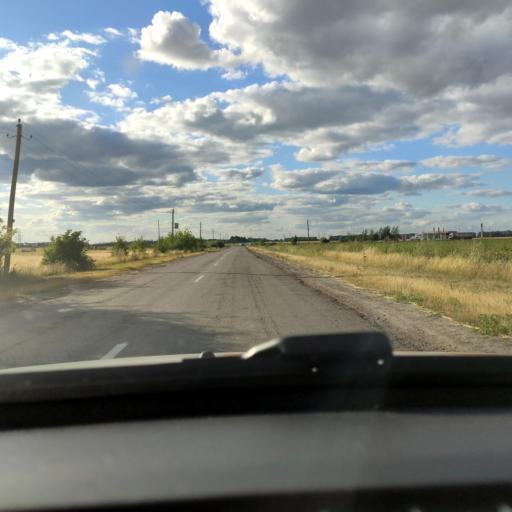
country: RU
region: Voronezj
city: Orlovo
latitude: 51.6747
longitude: 39.6841
